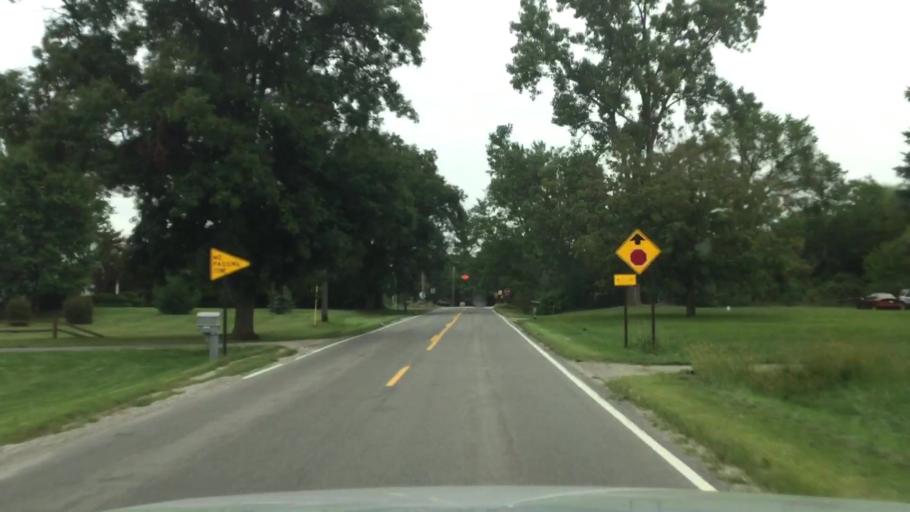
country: US
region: Michigan
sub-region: Washtenaw County
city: Milan
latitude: 42.1547
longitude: -83.6531
